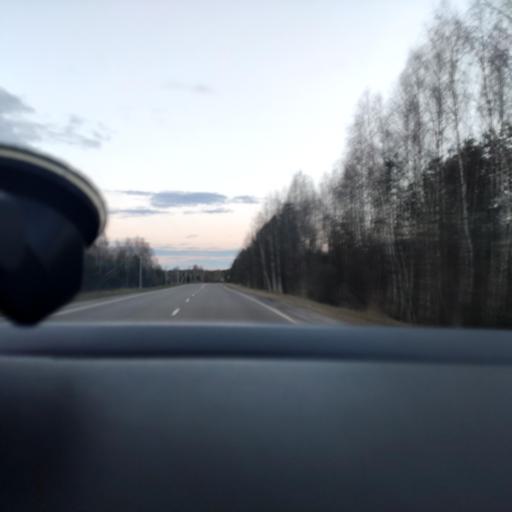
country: RU
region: Moskovskaya
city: Shaturtorf
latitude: 55.4540
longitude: 39.4506
